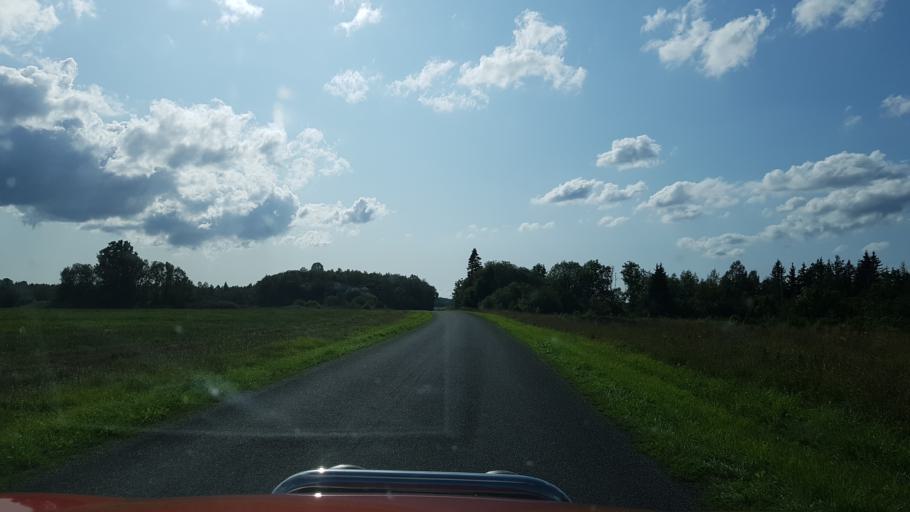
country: EE
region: Harju
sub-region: Paldiski linn
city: Paldiski
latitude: 59.2057
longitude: 23.9896
